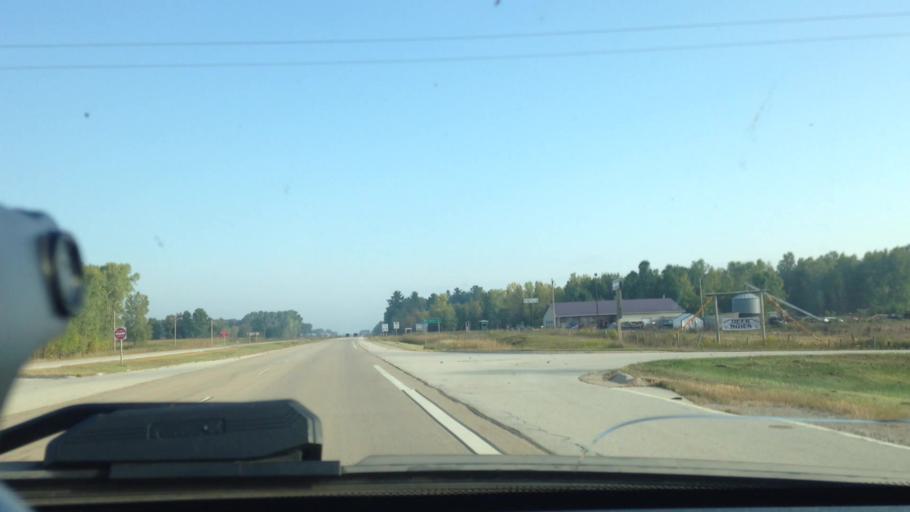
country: US
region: Wisconsin
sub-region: Oconto County
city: Oconto Falls
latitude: 45.0217
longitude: -88.0449
